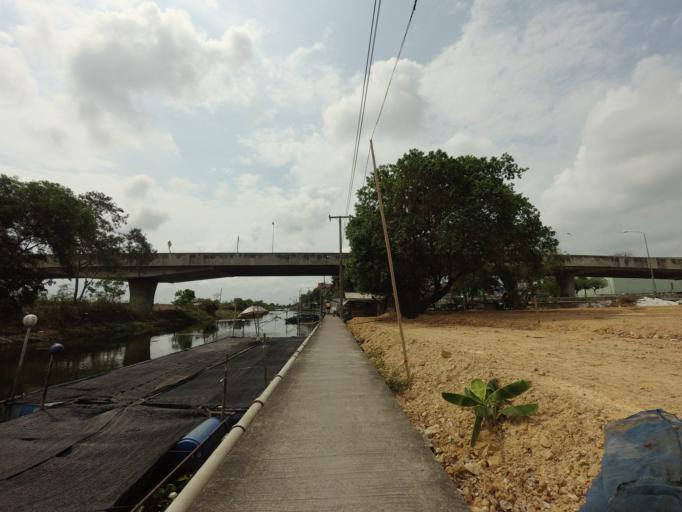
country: TH
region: Bangkok
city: Lat Krabang
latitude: 13.6726
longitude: 100.7254
